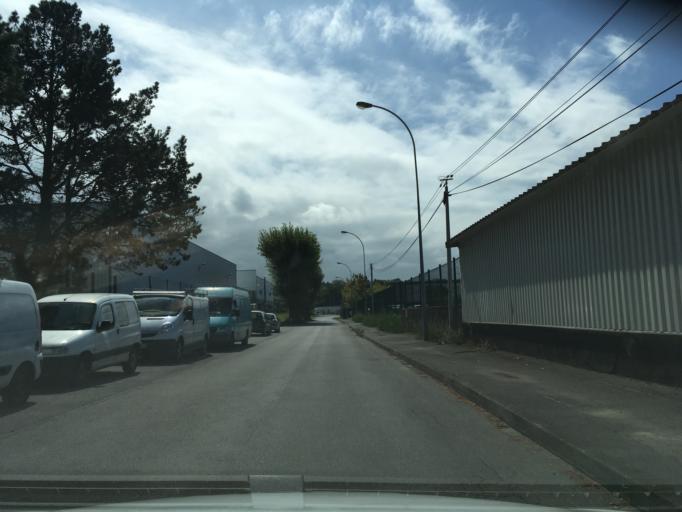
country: FR
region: Aquitaine
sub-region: Departement des Pyrenees-Atlantiques
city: Bayonne
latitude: 43.4924
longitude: -1.4566
